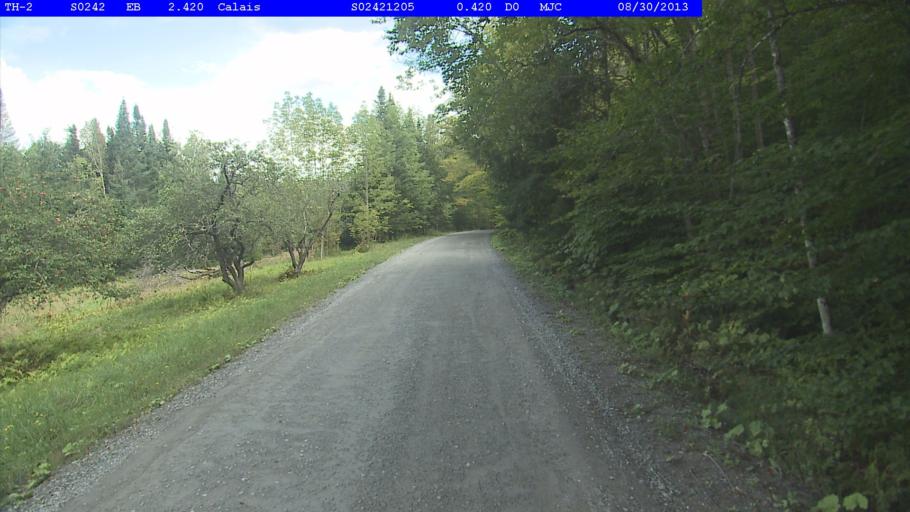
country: US
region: Vermont
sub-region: Washington County
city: Montpelier
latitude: 44.3894
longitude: -72.5122
